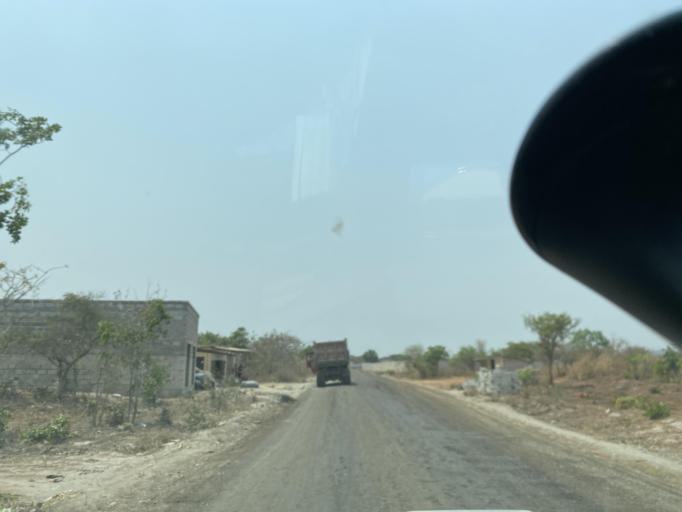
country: ZM
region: Lusaka
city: Lusaka
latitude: -15.5533
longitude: 28.4434
